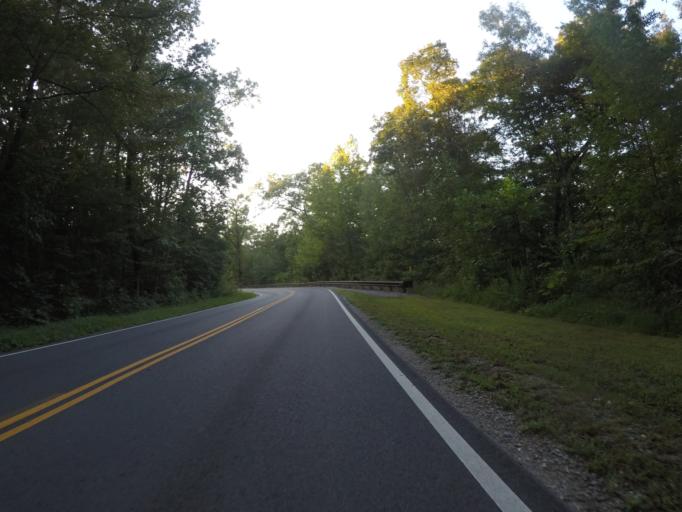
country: US
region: Ohio
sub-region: Lawrence County
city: Ironton
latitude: 38.6118
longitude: -82.6070
